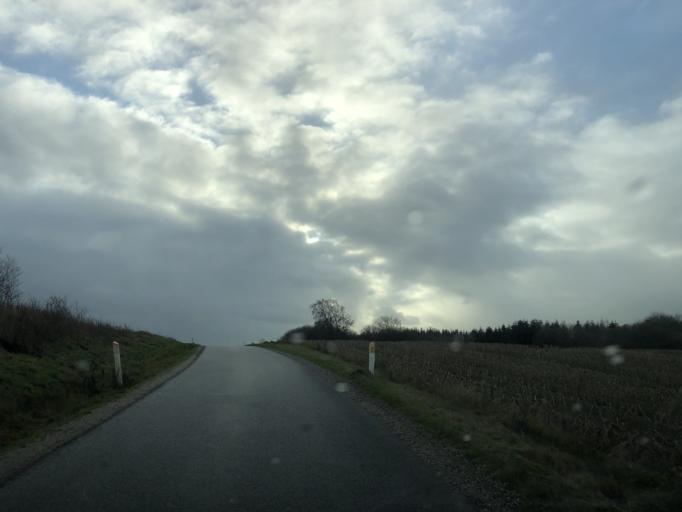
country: DK
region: North Denmark
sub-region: Rebild Kommune
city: Stovring
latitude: 56.9130
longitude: 9.7798
